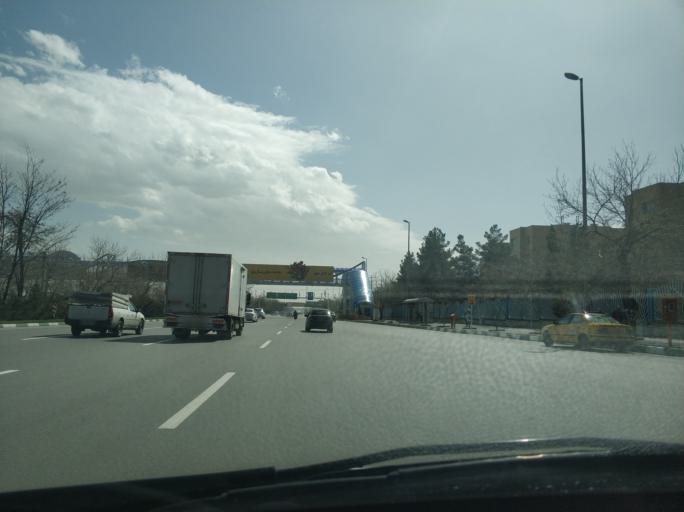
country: IR
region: Razavi Khorasan
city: Torqabeh
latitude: 36.3412
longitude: 59.4565
